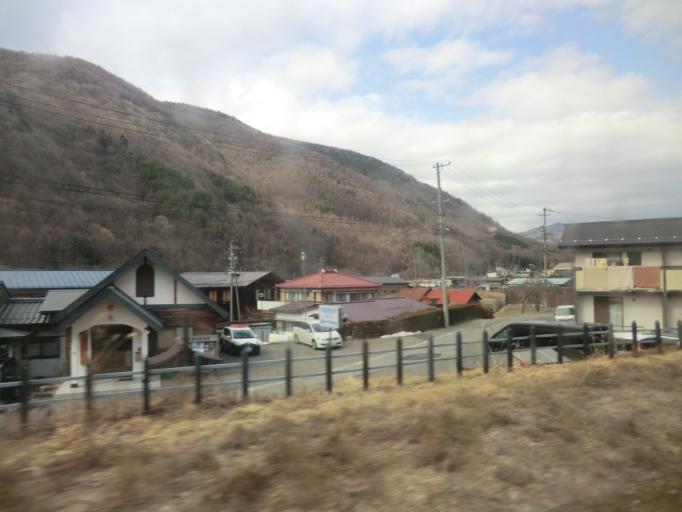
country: JP
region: Nagano
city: Ina
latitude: 35.9310
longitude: 137.7845
